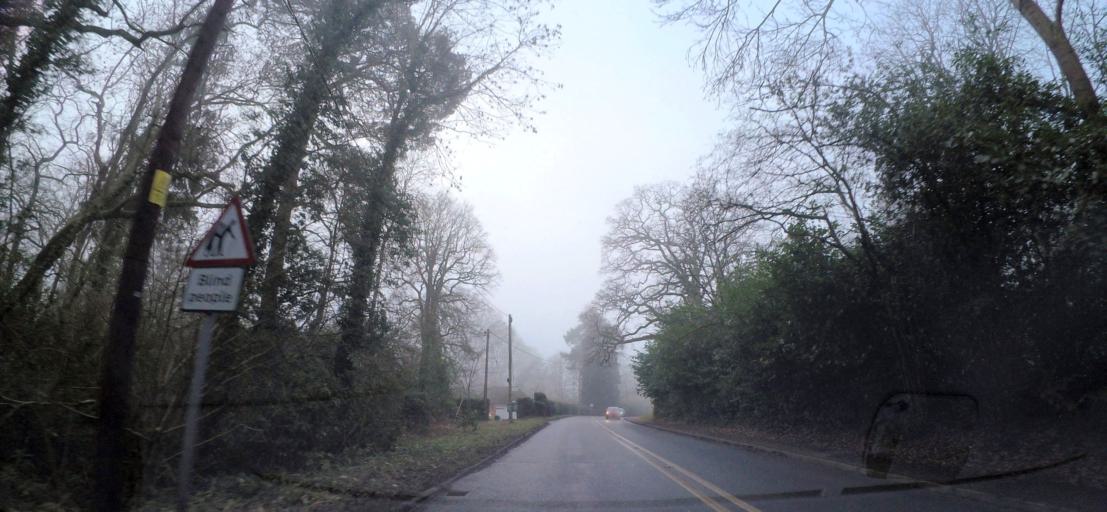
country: GB
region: England
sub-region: West Berkshire
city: Stratfield Mortimer
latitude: 51.4053
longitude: -1.0454
